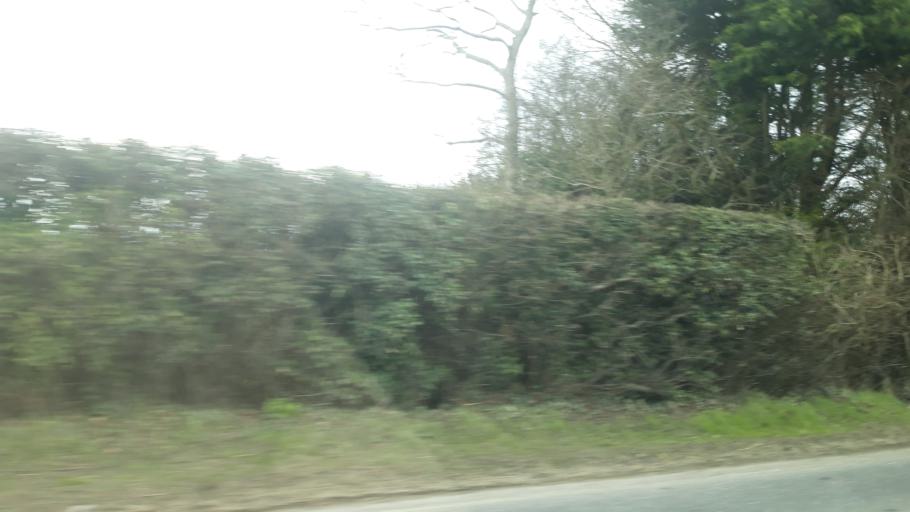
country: IE
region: Leinster
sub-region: Kildare
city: Clane
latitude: 53.3034
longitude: -6.6676
